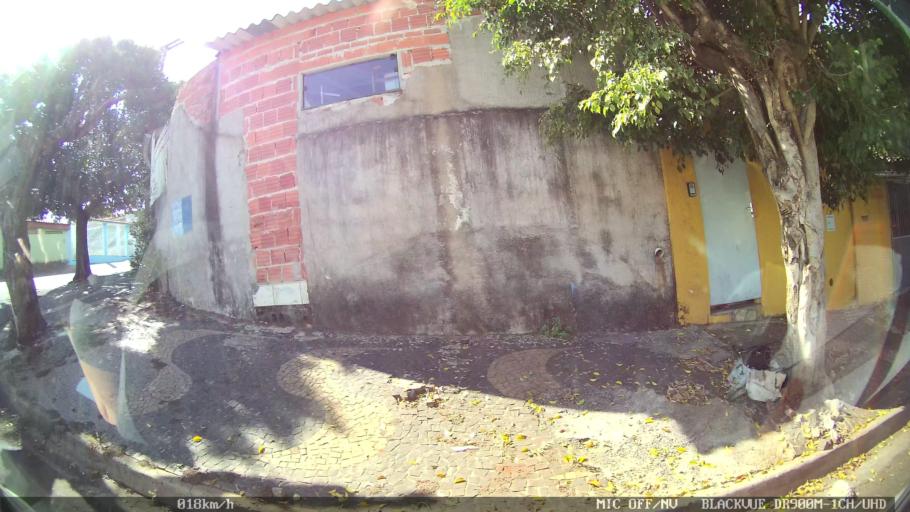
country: BR
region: Sao Paulo
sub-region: Santa Barbara D'Oeste
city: Santa Barbara d'Oeste
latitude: -22.7359
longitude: -47.3883
